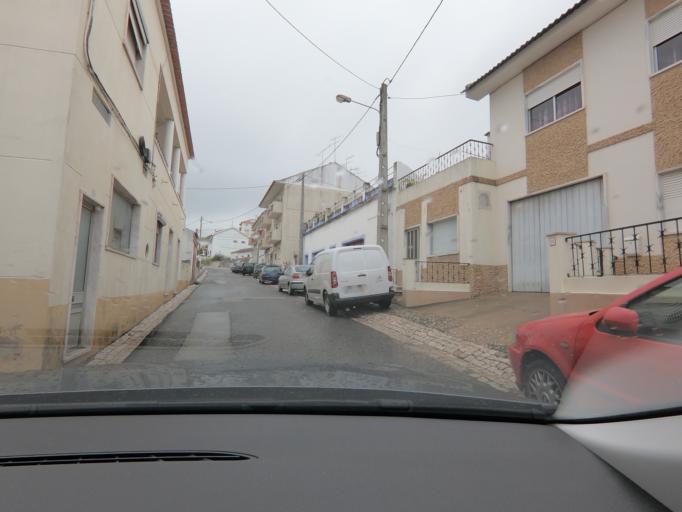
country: PT
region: Lisbon
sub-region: Alenquer
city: Alenquer
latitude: 39.0484
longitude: -9.0028
